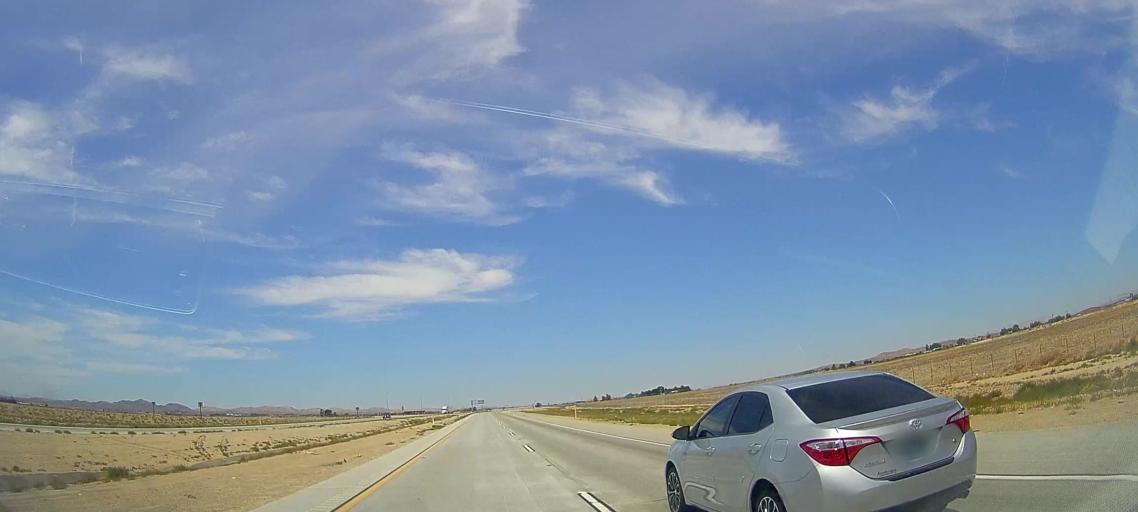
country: US
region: California
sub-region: San Bernardino County
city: Lenwood
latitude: 34.9150
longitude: -117.1215
